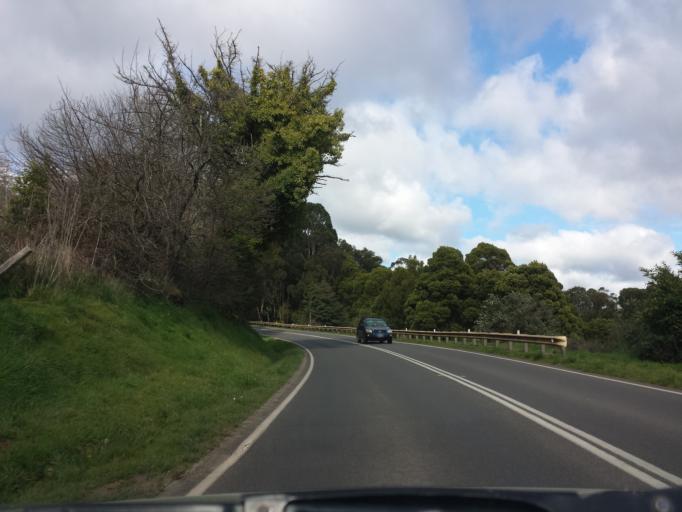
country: AU
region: Victoria
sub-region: Yarra Ranges
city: Kalorama
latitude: -37.8158
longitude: 145.4065
